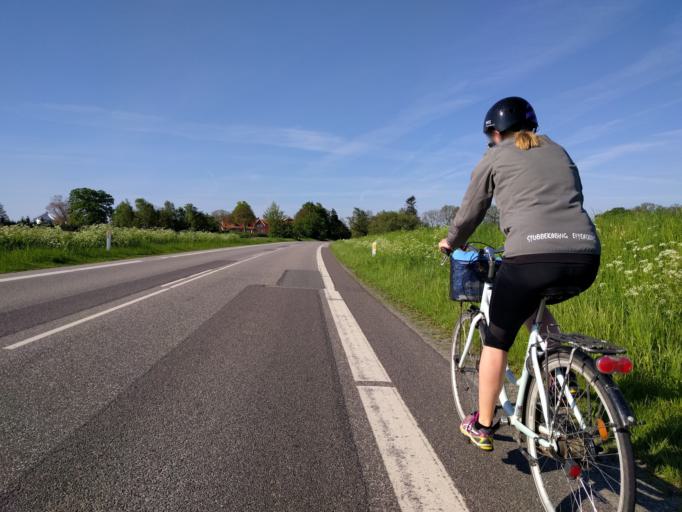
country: DK
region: Zealand
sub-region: Guldborgsund Kommune
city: Stubbekobing
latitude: 54.8487
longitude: 12.0128
